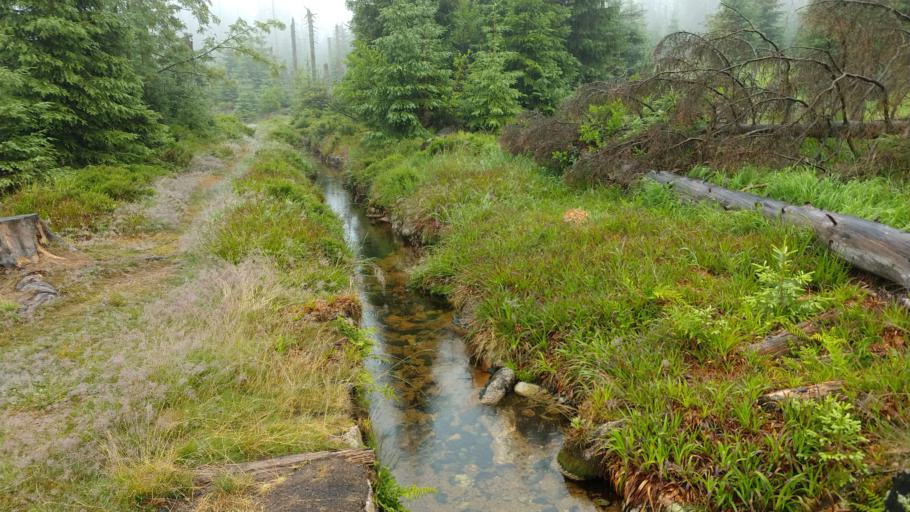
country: DE
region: Lower Saxony
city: Bad Harzburg
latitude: 51.7964
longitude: 10.5582
